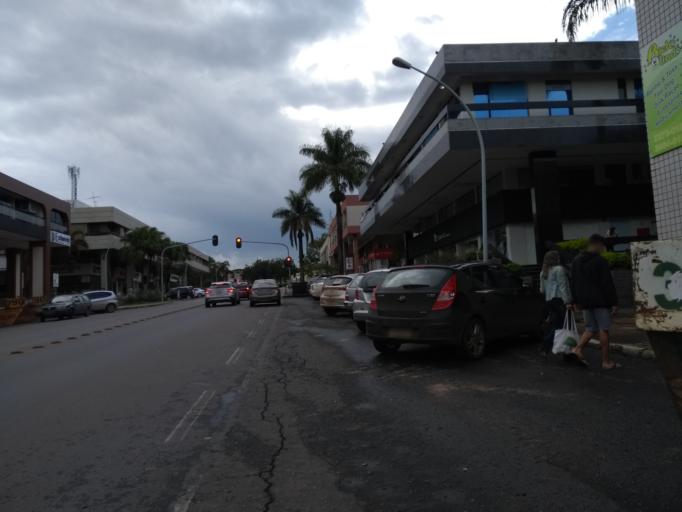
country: BR
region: Federal District
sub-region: Brasilia
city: Brasilia
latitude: -15.7524
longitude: -47.8892
